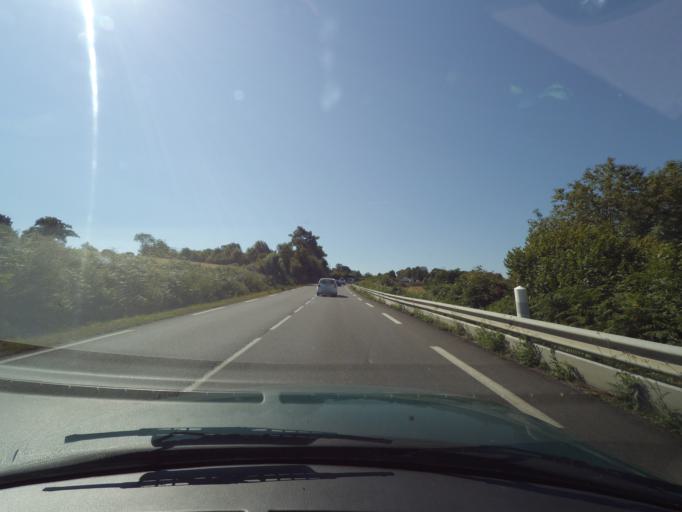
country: FR
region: Limousin
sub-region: Departement de la Haute-Vienne
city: Peyrat-de-Bellac
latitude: 46.1607
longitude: 0.9598
